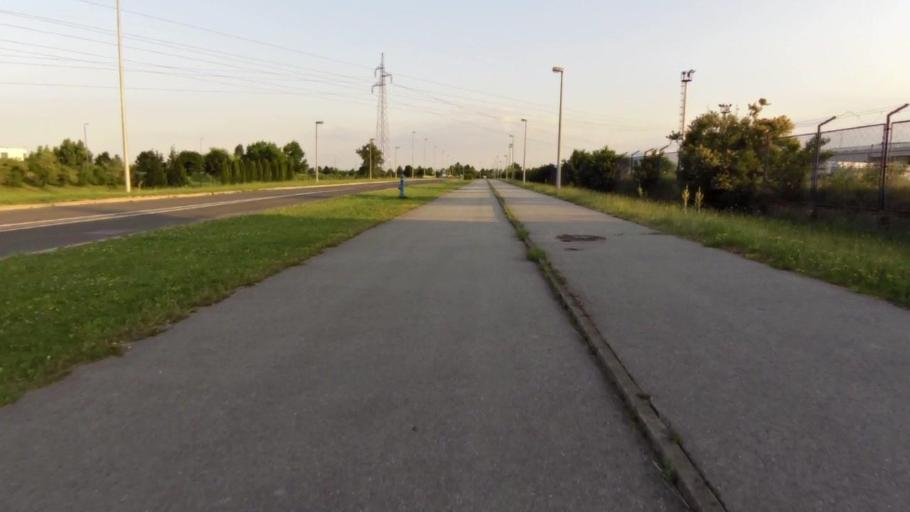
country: HR
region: Zagrebacka
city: Micevec
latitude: 45.7912
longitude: 16.0790
